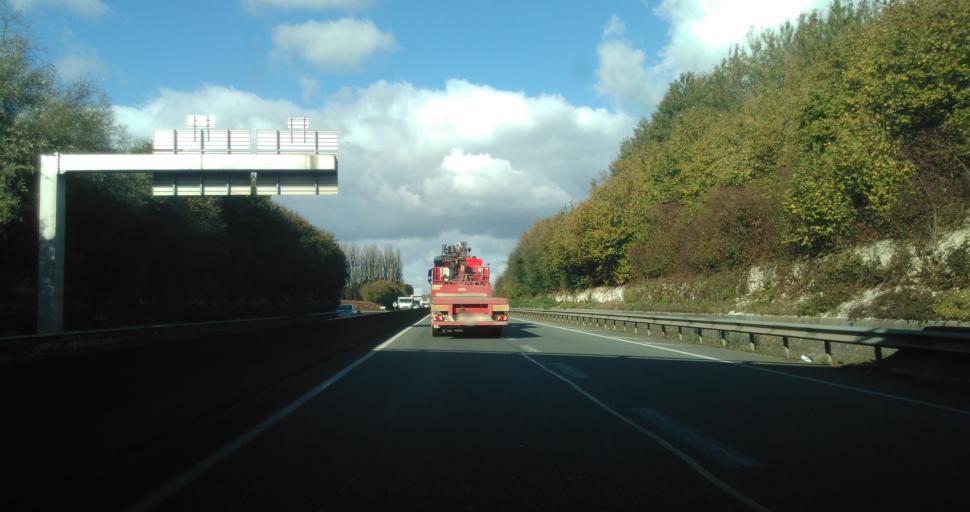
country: FR
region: Nord-Pas-de-Calais
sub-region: Departement du Pas-de-Calais
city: Dainville
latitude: 50.3030
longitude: 2.7246
